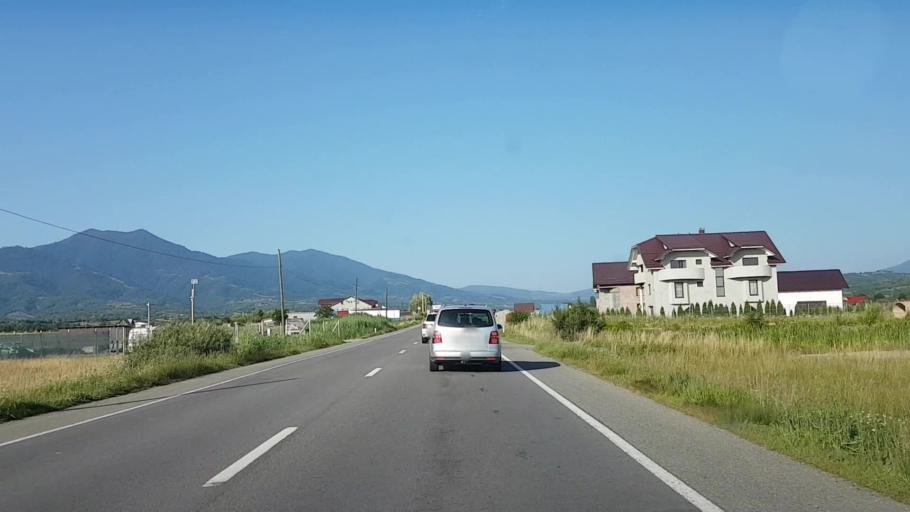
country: RO
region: Bistrita-Nasaud
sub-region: Comuna Josenii Bargaului
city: Josenii Bargaului
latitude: 47.2041
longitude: 24.6507
